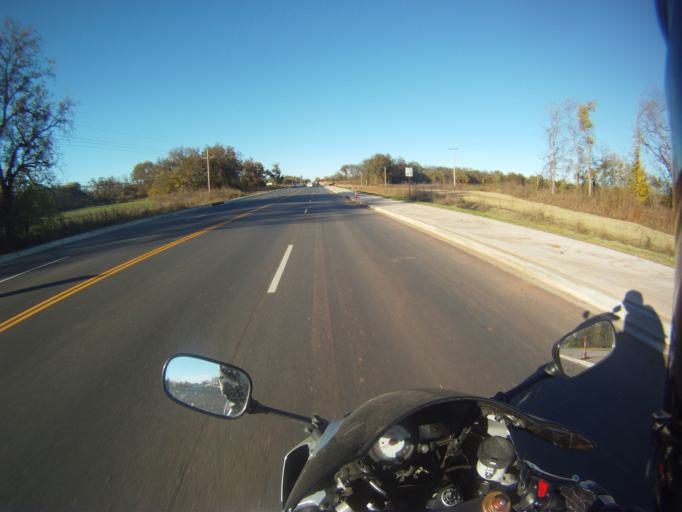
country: US
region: Oklahoma
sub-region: Payne County
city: Stillwater
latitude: 36.1243
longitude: -97.1231
